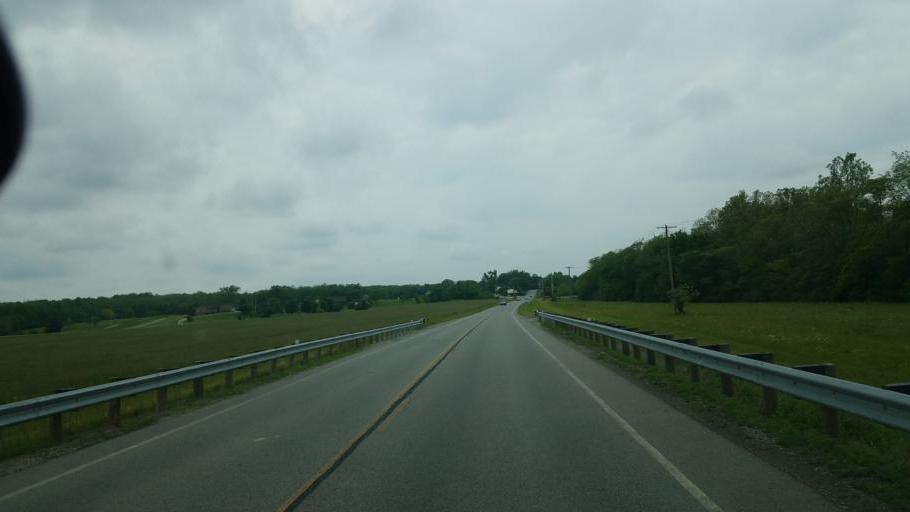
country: US
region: Ohio
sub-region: Delaware County
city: Delaware
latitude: 40.3219
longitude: -83.1702
